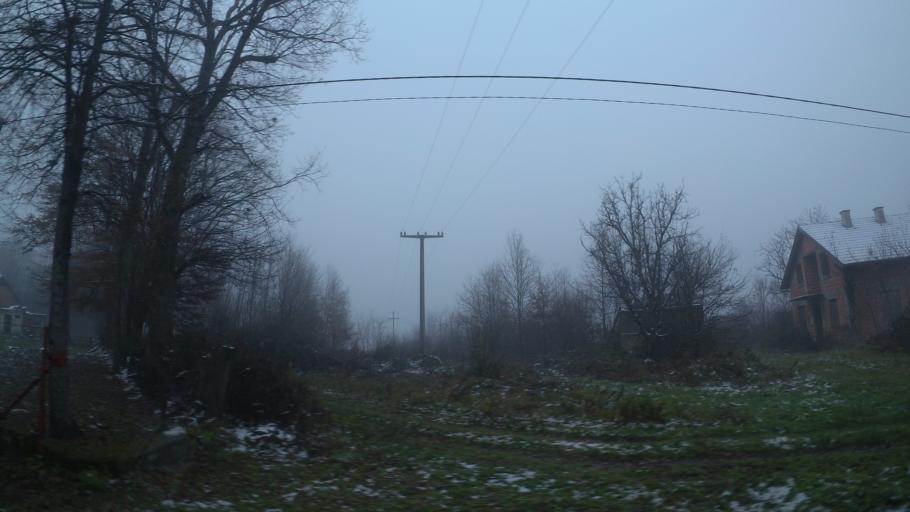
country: HR
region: Sisacko-Moslavacka
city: Glina
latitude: 45.3167
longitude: 16.0262
